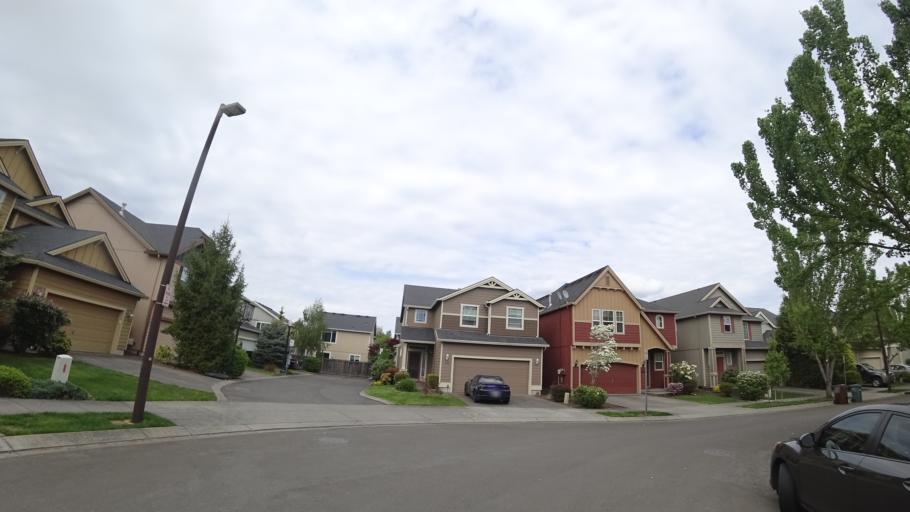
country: US
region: Oregon
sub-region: Washington County
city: Hillsboro
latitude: 45.4948
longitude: -122.9662
